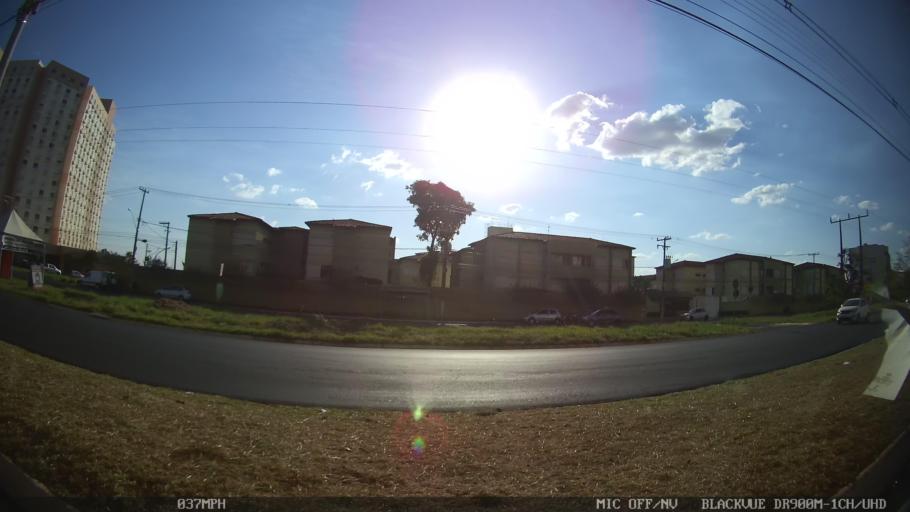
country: BR
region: Sao Paulo
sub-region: Ribeirao Preto
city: Ribeirao Preto
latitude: -21.1977
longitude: -47.7791
